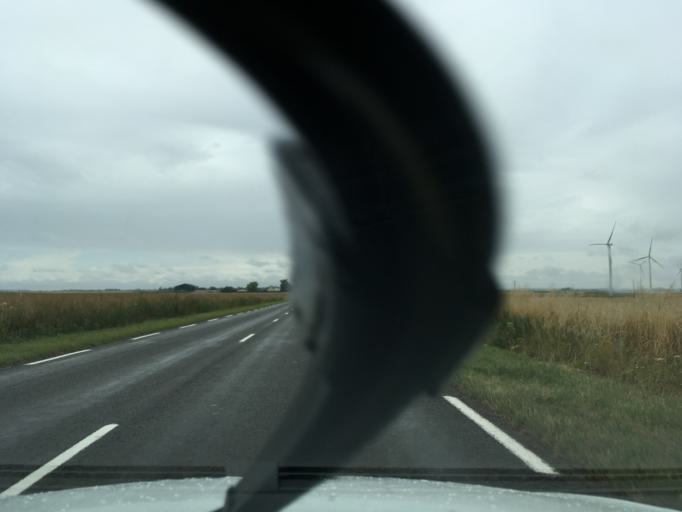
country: FR
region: Picardie
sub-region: Departement de l'Aisne
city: Esqueheries
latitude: 49.9311
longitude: 3.7108
